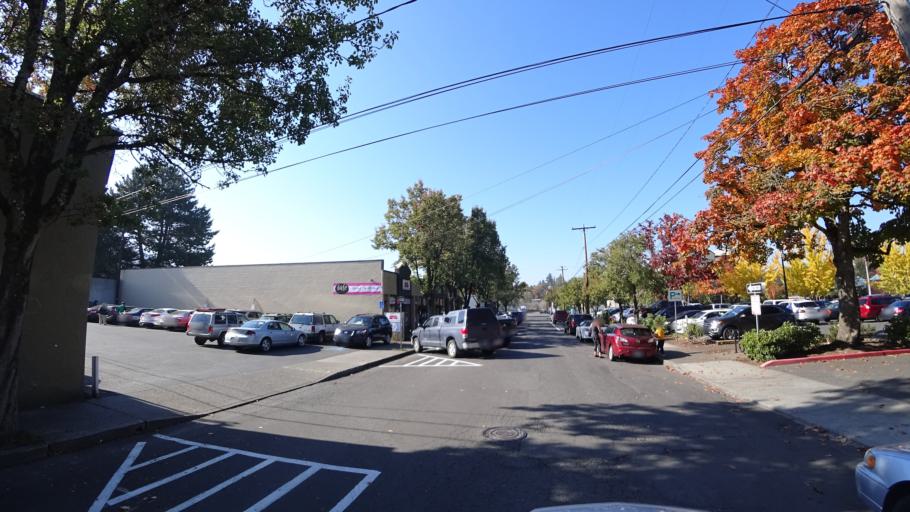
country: US
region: Oregon
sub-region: Multnomah County
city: Gresham
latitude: 45.4990
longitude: -122.4313
